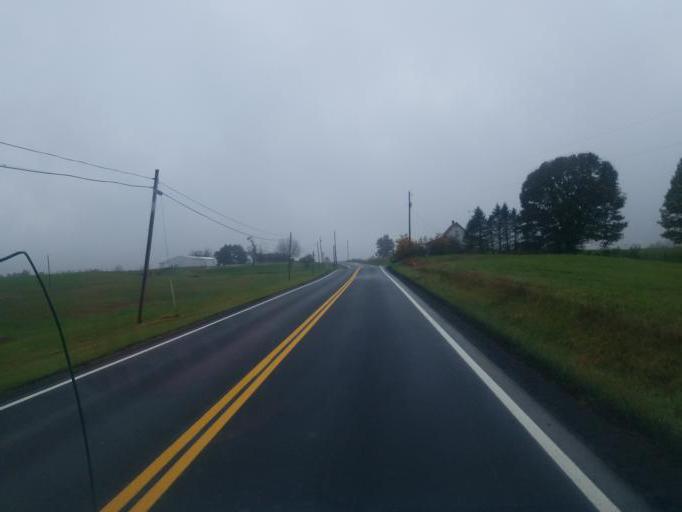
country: US
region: Ohio
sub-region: Morgan County
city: McConnelsville
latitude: 39.5599
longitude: -81.8298
